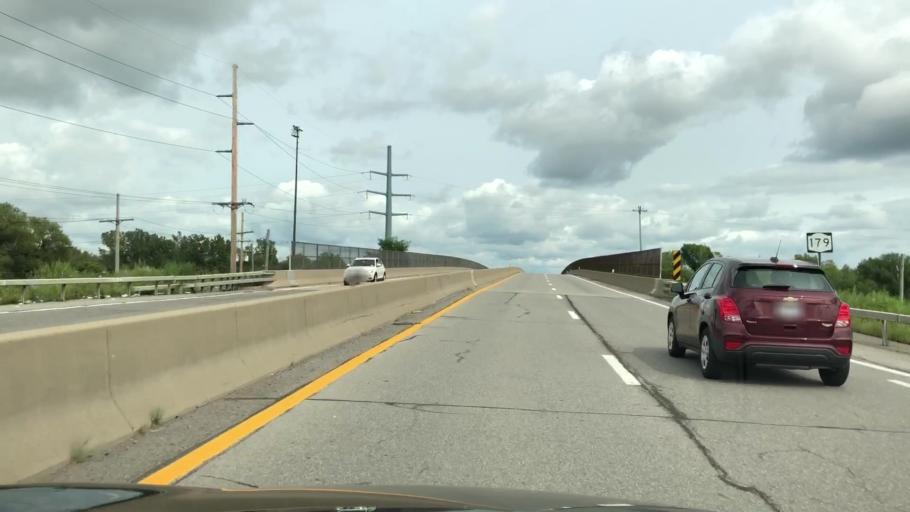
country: US
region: New York
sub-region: Erie County
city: Blasdell
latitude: 42.7899
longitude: -78.8380
